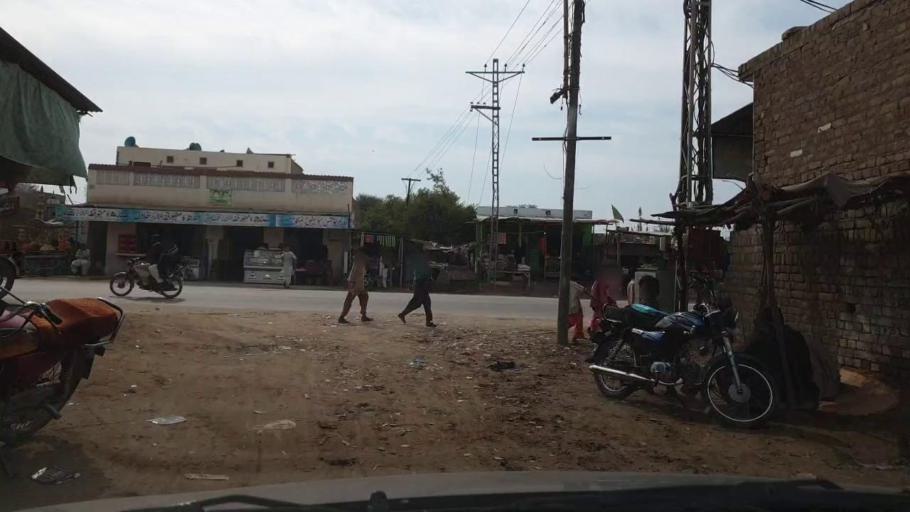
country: PK
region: Sindh
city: Sinjhoro
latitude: 26.0971
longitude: 68.8582
